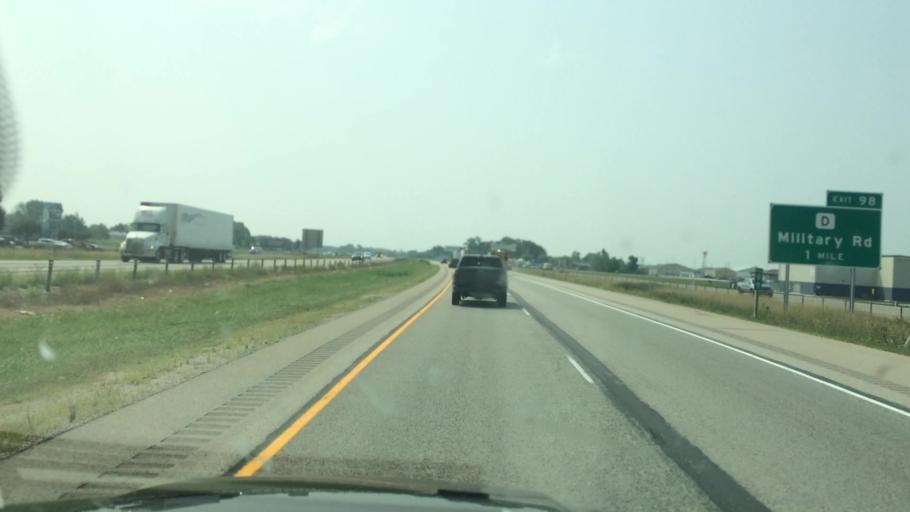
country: US
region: Wisconsin
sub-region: Fond du Lac County
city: North Fond du Lac
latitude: 43.7741
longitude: -88.4824
